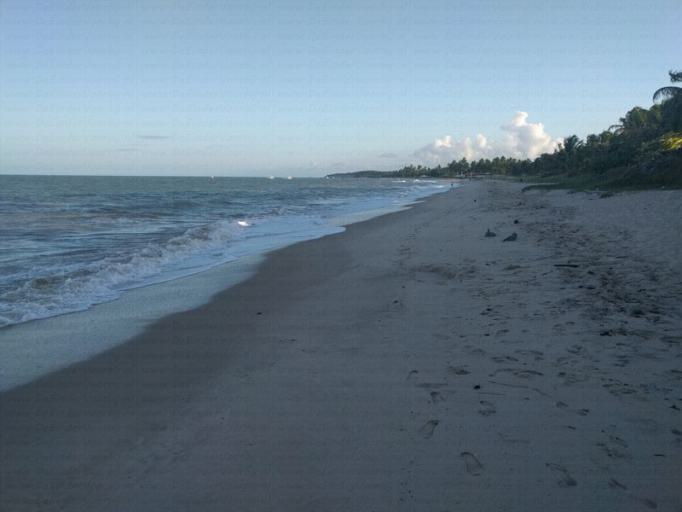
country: BR
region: Paraiba
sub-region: Joao Pessoa
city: Joao Pessoa
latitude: -7.1599
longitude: -34.7946
